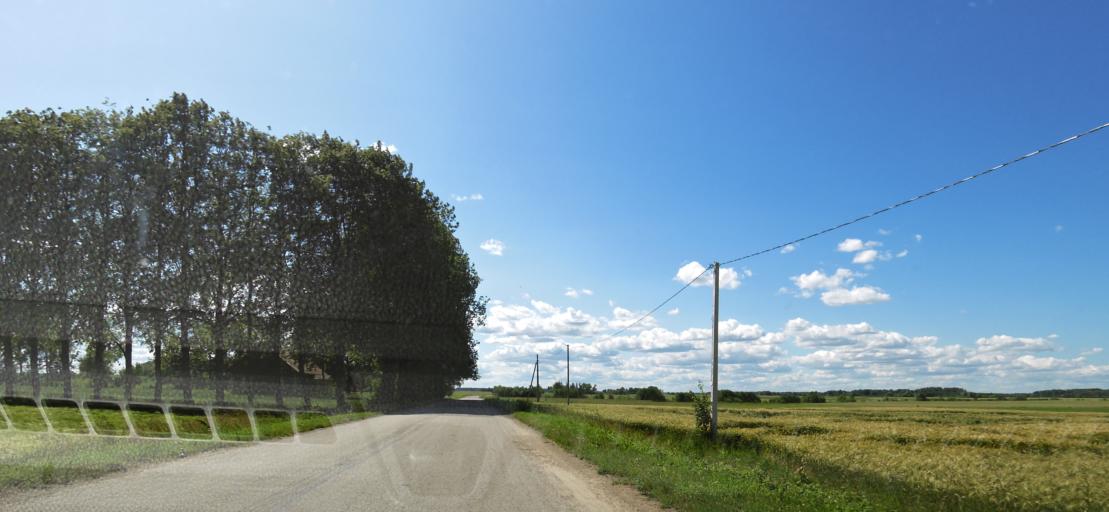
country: LV
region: Bauskas Rajons
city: Bauska
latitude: 56.2395
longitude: 24.2260
